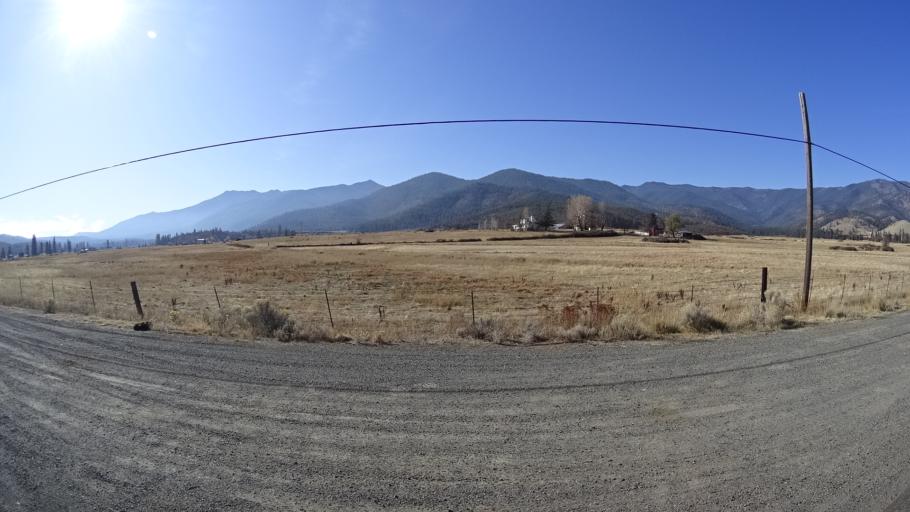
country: US
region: California
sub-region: Siskiyou County
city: Weed
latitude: 41.4421
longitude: -122.4385
